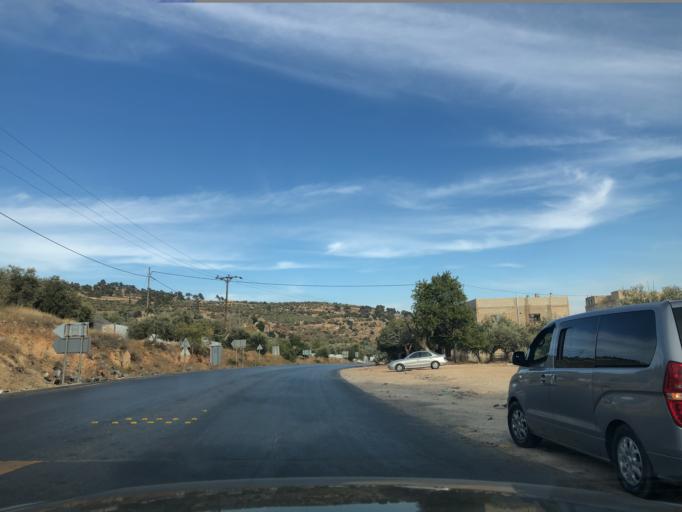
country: JO
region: Irbid
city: Al Kittah
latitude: 32.2913
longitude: 35.8466
